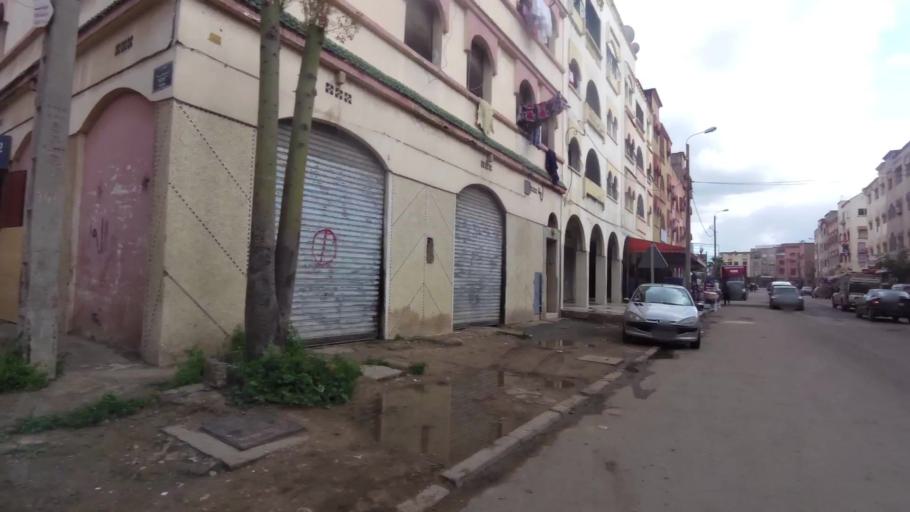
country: MA
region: Chaouia-Ouardigha
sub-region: Settat Province
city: Berrechid
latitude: 33.2661
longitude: -7.5766
